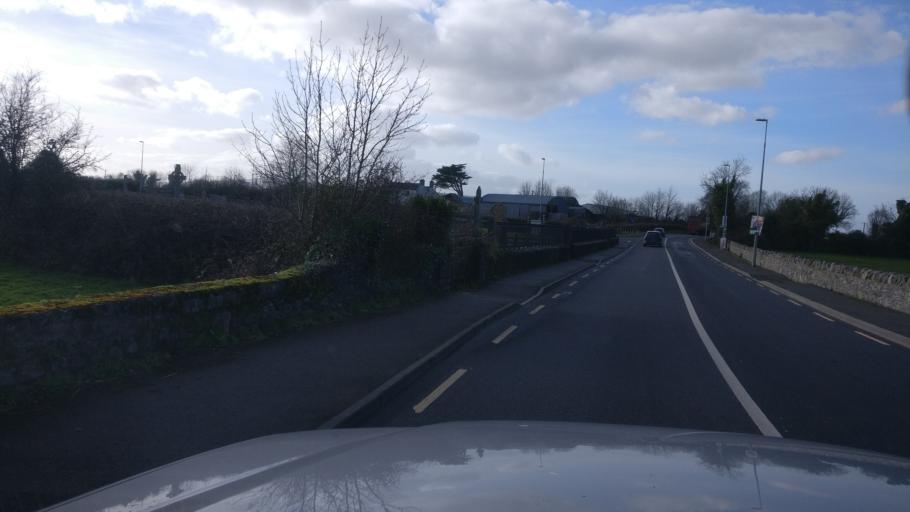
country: IE
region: Leinster
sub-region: Laois
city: Mountmellick
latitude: 53.1240
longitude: -7.3343
